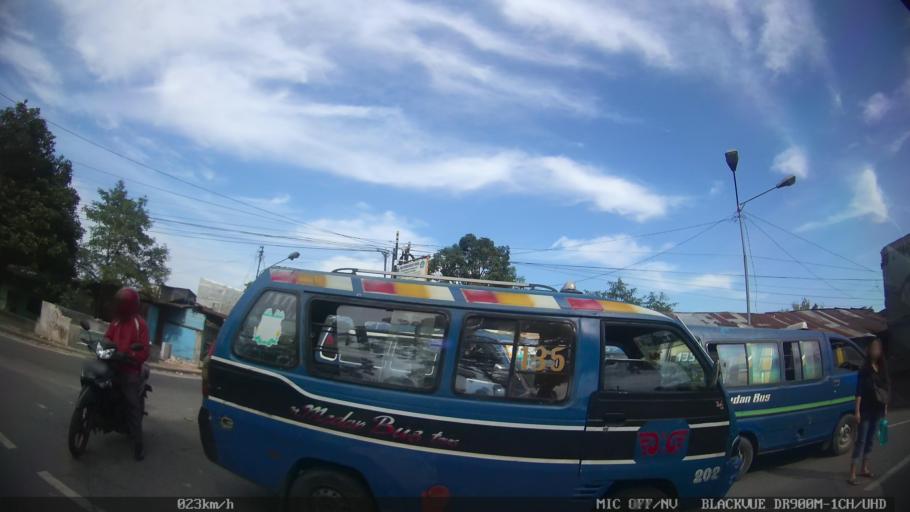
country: ID
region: North Sumatra
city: Sunggal
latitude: 3.6125
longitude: 98.6276
